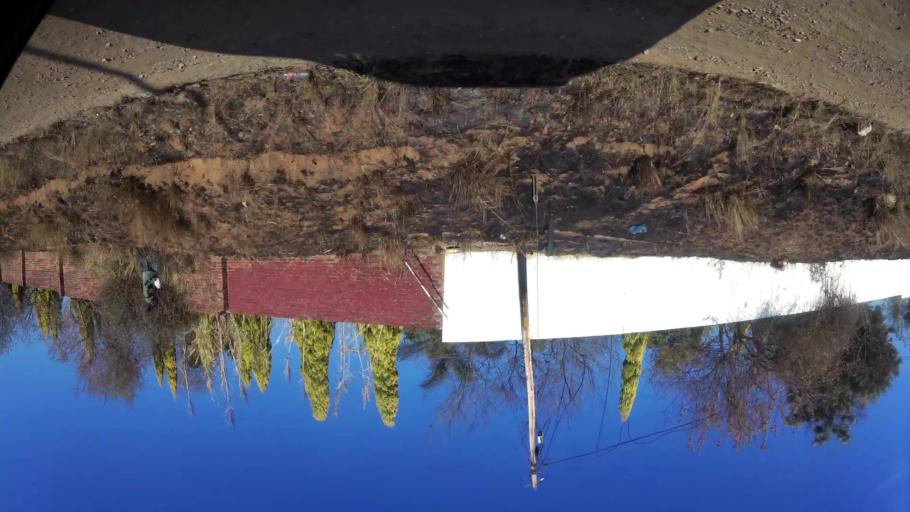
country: ZA
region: Gauteng
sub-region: West Rand District Municipality
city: Muldersdriseloop
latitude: -26.0261
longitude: 27.8687
